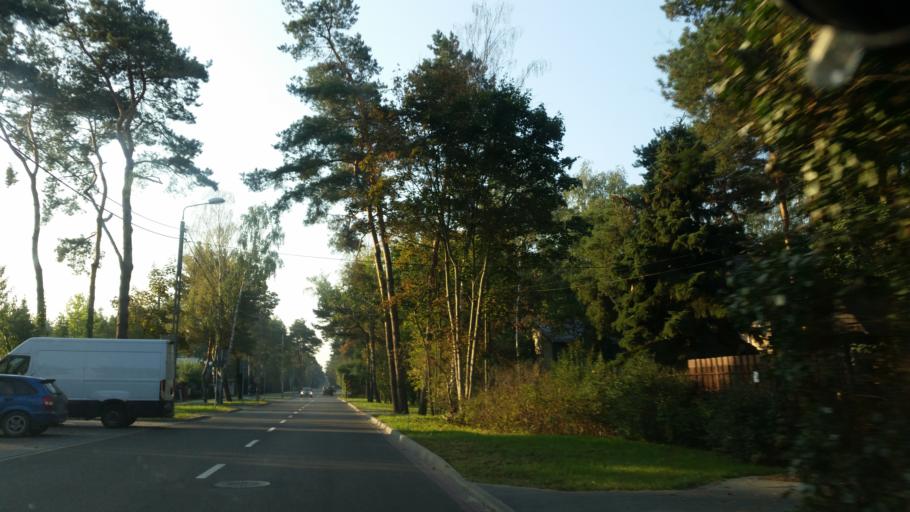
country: PL
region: Masovian Voivodeship
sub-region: Powiat otwocki
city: Jozefow
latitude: 52.1439
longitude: 21.2147
